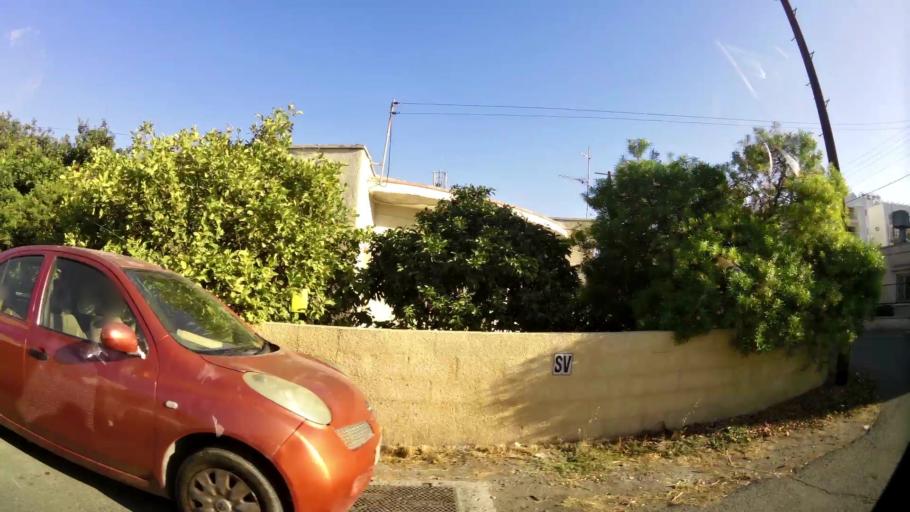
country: CY
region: Larnaka
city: Larnaca
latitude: 34.9205
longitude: 33.6188
